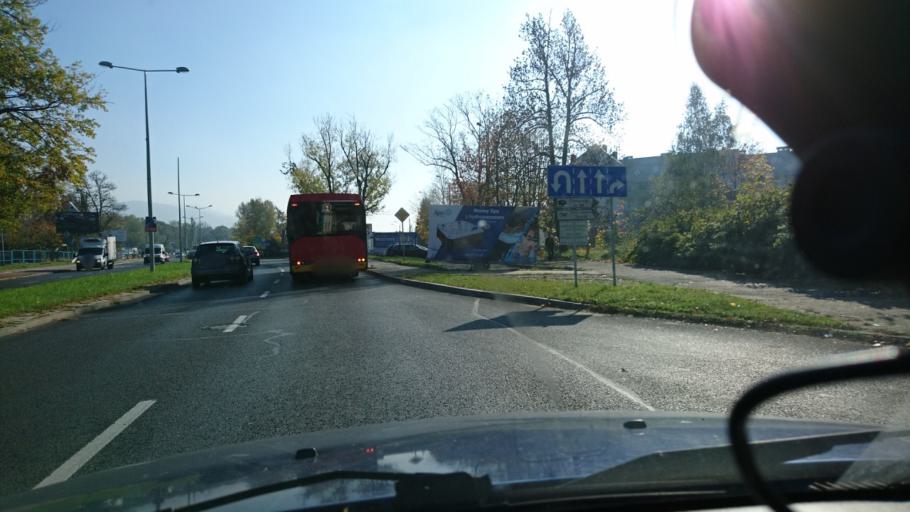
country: PL
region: Silesian Voivodeship
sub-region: Bielsko-Biala
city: Bielsko-Biala
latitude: 49.8041
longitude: 19.0438
